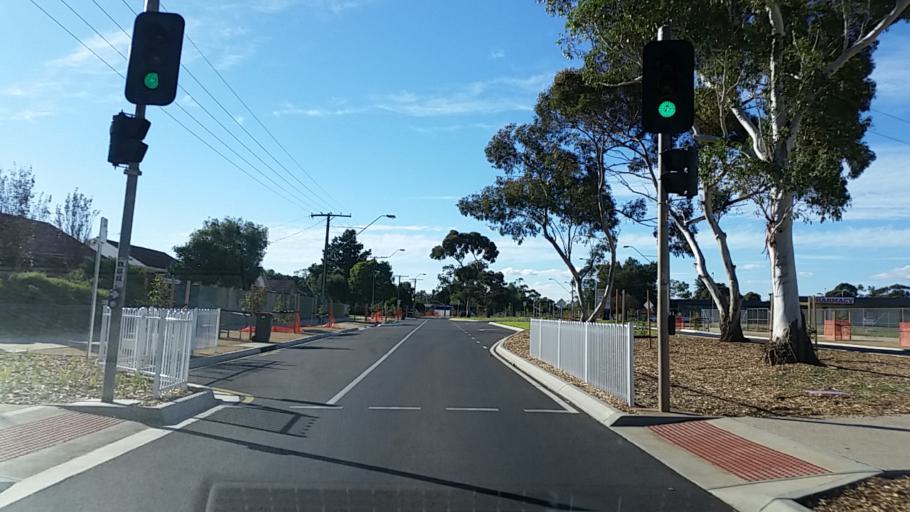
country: AU
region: South Australia
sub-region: Playford
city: Smithfield
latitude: -34.6865
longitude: 138.6703
